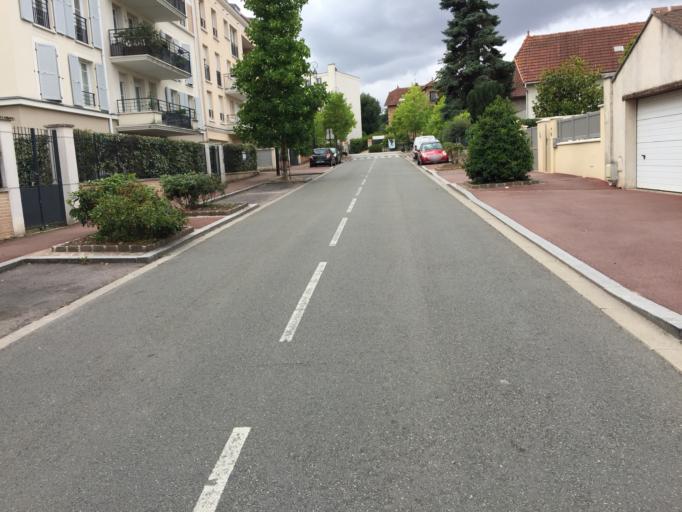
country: FR
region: Ile-de-France
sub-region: Departement des Yvelines
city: Les Clayes-sous-Bois
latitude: 48.8207
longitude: 1.9899
